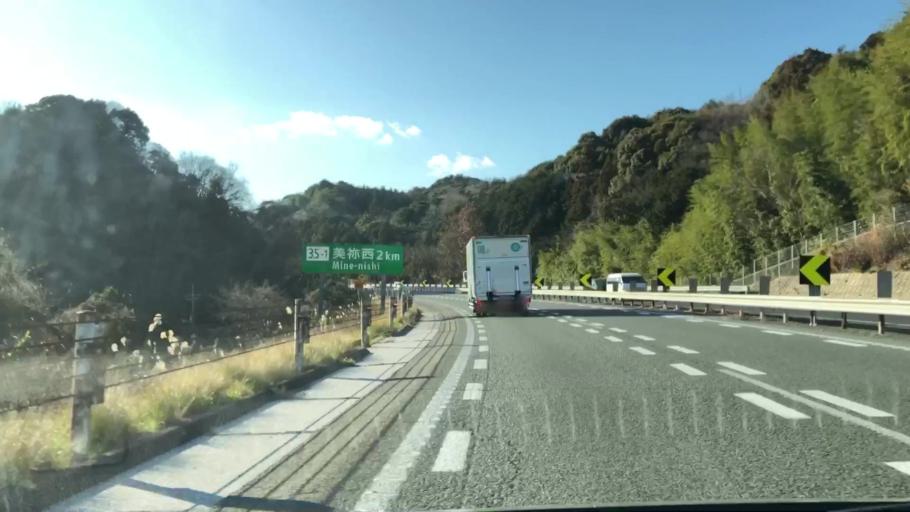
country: JP
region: Yamaguchi
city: Onoda
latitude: 34.1139
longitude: 131.1645
